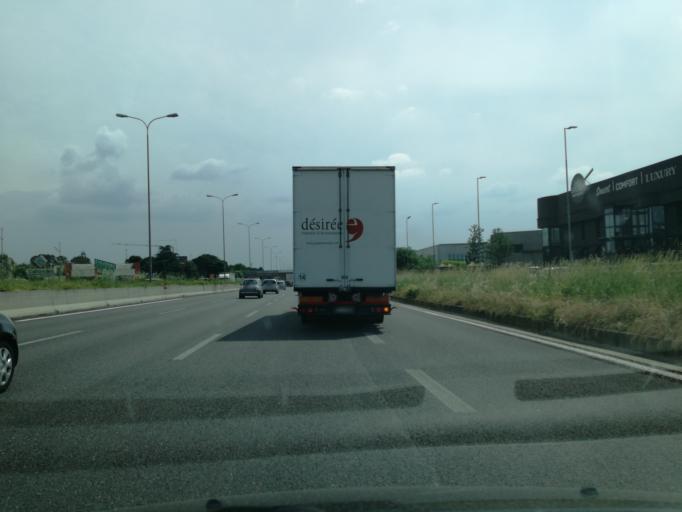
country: IT
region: Lombardy
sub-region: Provincia di Monza e Brianza
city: Verano Brianza
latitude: 45.6809
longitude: 9.2170
